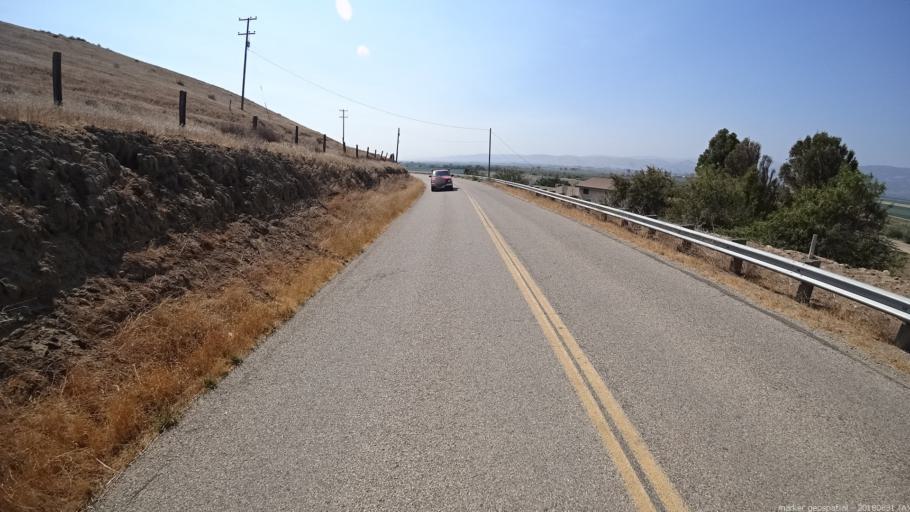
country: US
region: California
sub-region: Monterey County
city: Greenfield
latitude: 36.3877
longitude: -121.2480
